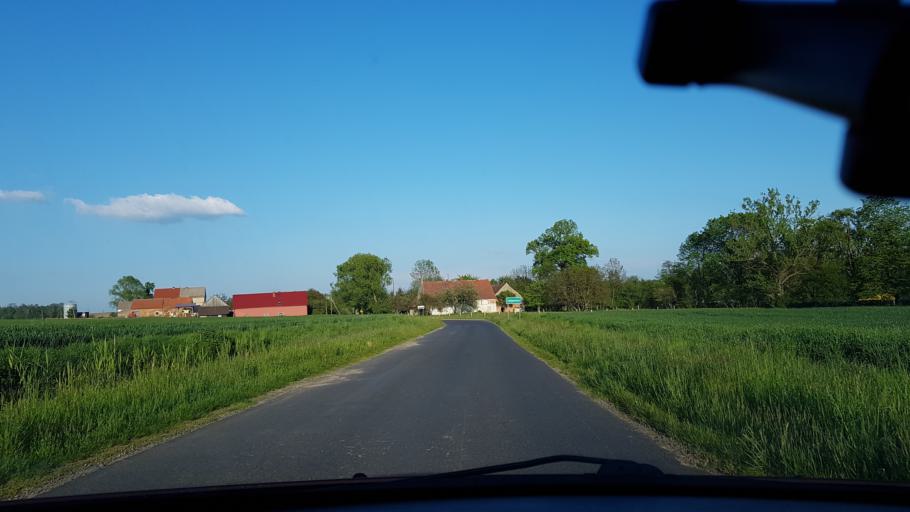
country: PL
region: Lower Silesian Voivodeship
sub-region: Powiat zabkowicki
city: Budzow
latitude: 50.6109
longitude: 16.7027
